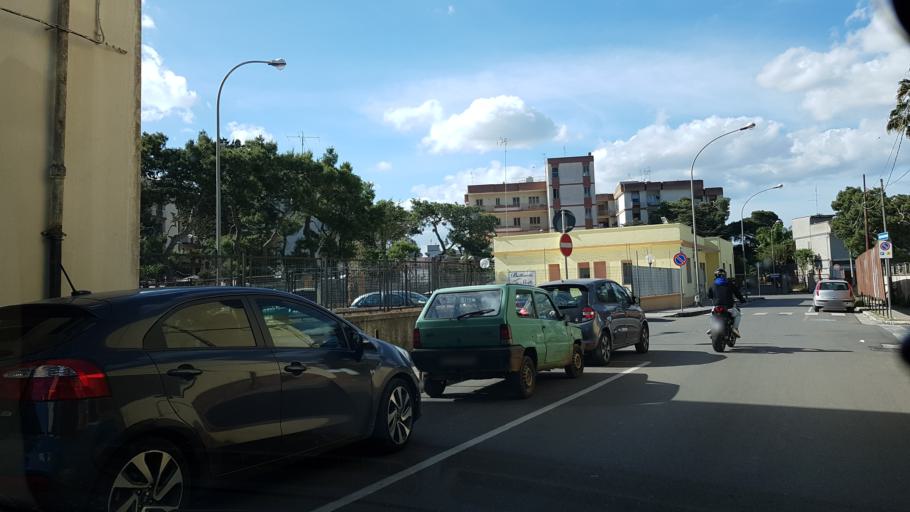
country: IT
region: Apulia
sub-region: Provincia di Brindisi
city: Mesagne
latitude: 40.5605
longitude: 17.8006
